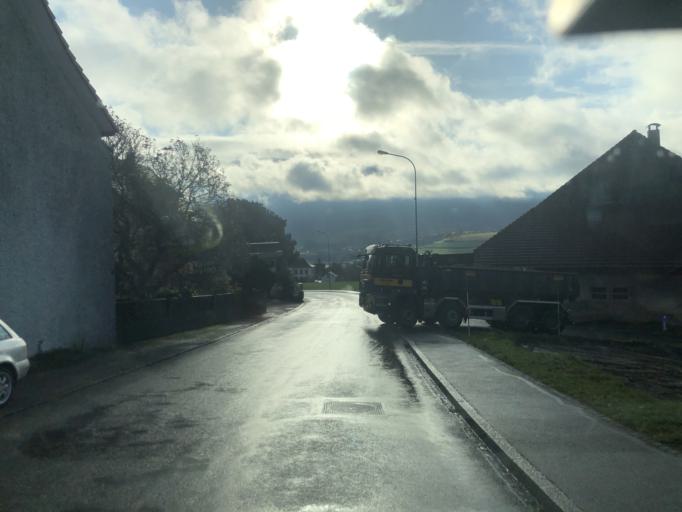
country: CH
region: Aargau
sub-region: Bezirk Baden
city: Unterehrendingen
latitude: 47.5220
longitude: 8.3586
